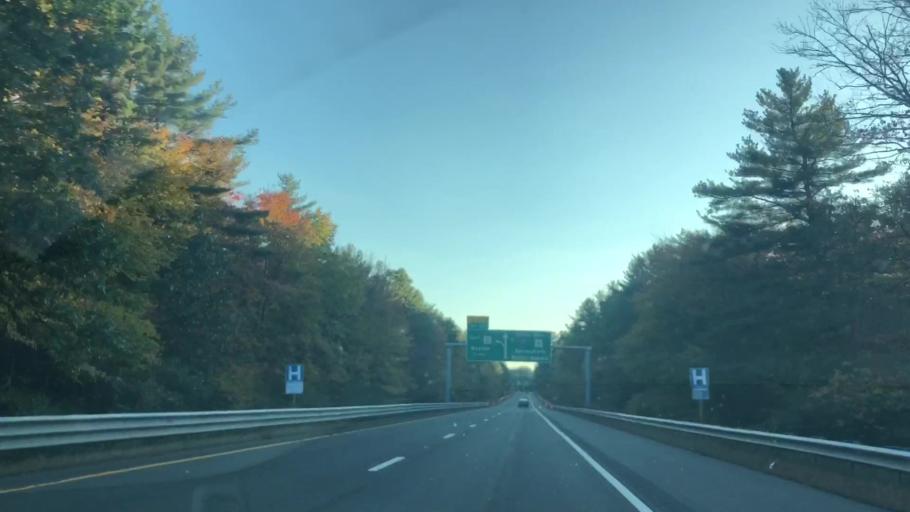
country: US
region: Massachusetts
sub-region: Franklin County
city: Turners Falls
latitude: 42.6263
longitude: -72.5856
